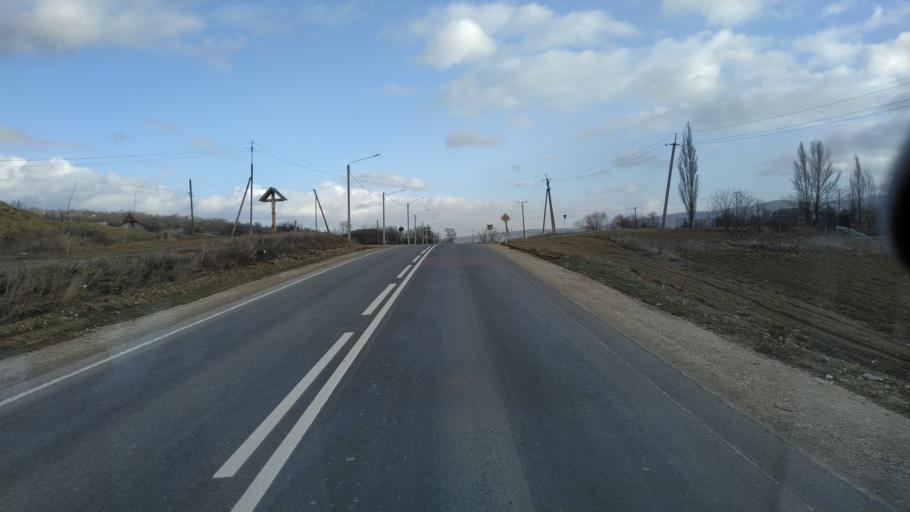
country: MD
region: Calarasi
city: Calarasi
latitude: 47.3236
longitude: 28.1052
